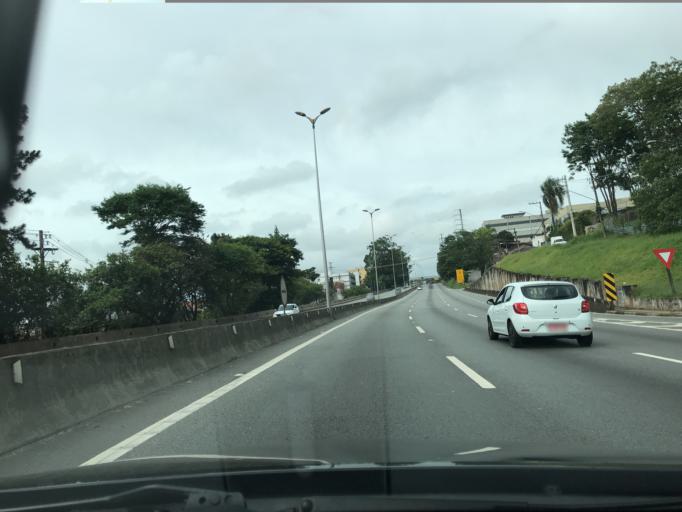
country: BR
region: Sao Paulo
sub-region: Embu
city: Embu
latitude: -23.5970
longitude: -46.8413
